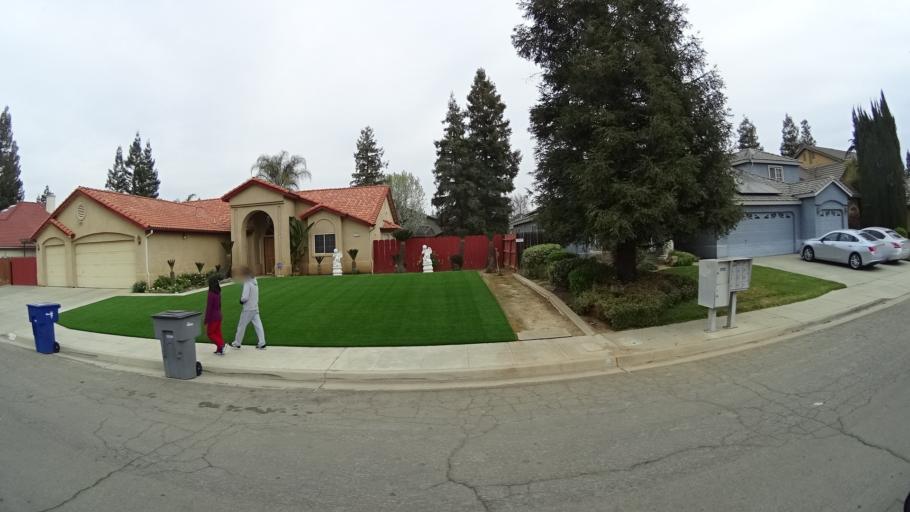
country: US
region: California
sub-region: Fresno County
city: Clovis
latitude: 36.8556
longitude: -119.7449
